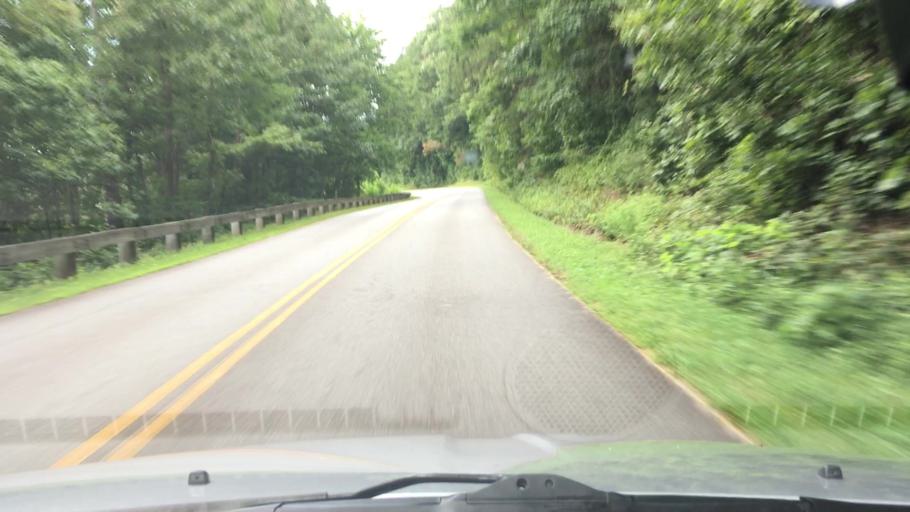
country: US
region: North Carolina
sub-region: Buncombe County
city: Asheville
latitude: 35.6189
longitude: -82.4924
